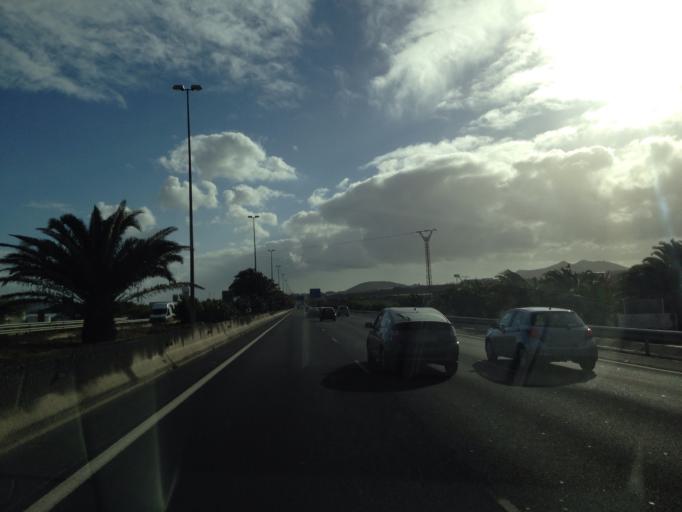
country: ES
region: Canary Islands
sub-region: Provincia de Las Palmas
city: Ingenio
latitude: 27.9336
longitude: -15.3939
